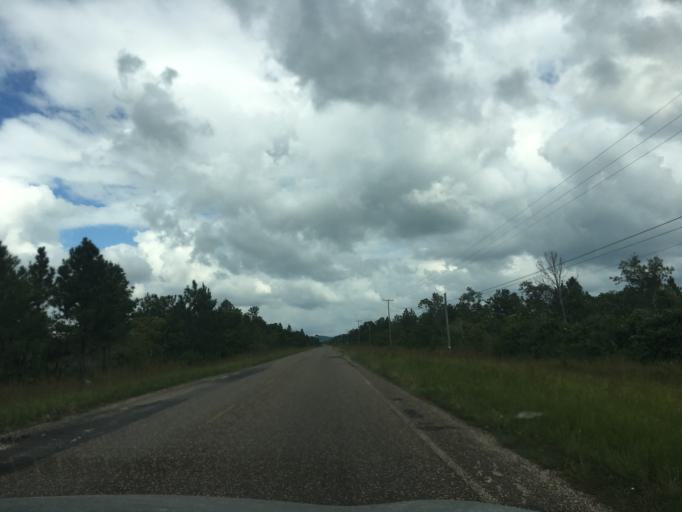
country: BZ
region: Stann Creek
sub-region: Dangriga
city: Dangriga
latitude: 16.9056
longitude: -88.3410
